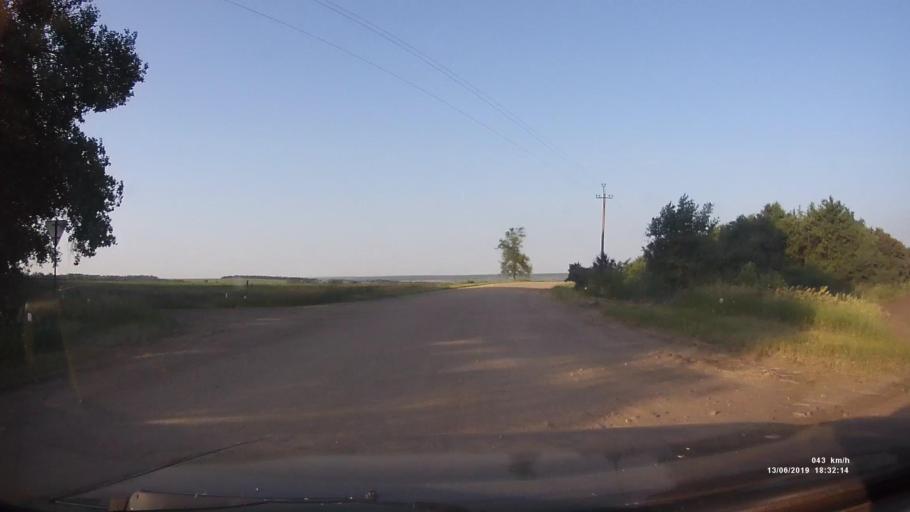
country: RU
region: Rostov
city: Kazanskaya
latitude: 49.8700
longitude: 41.3660
